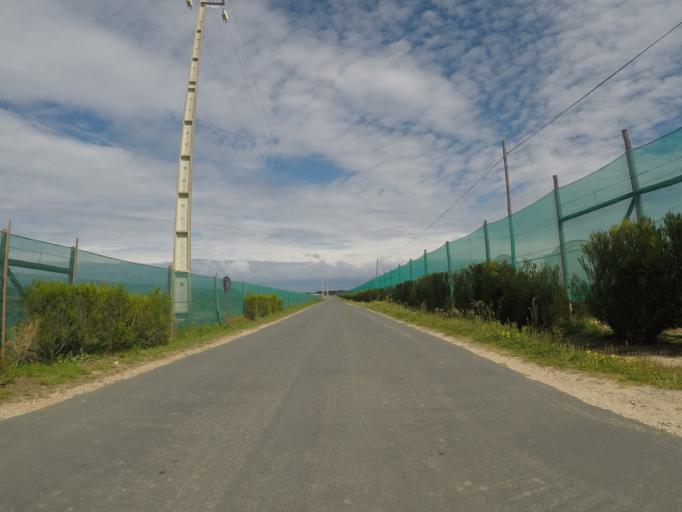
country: PT
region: Beja
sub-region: Odemira
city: Sao Teotonio
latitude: 37.4835
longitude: -8.7698
